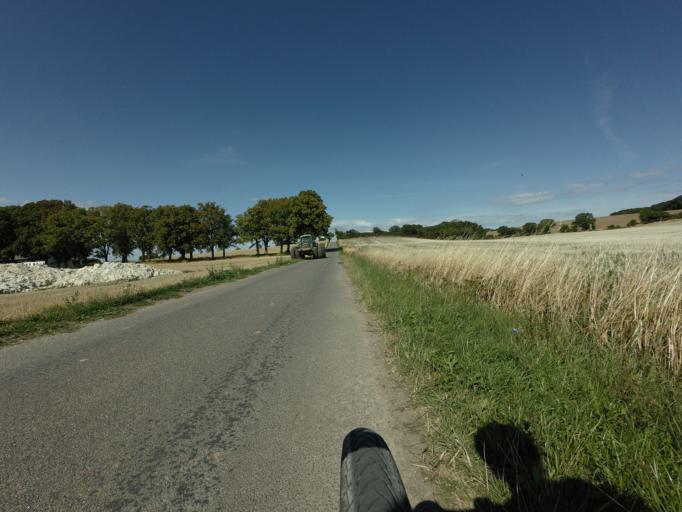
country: DK
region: Zealand
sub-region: Vordingborg Kommune
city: Stege
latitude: 55.0137
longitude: 12.4597
